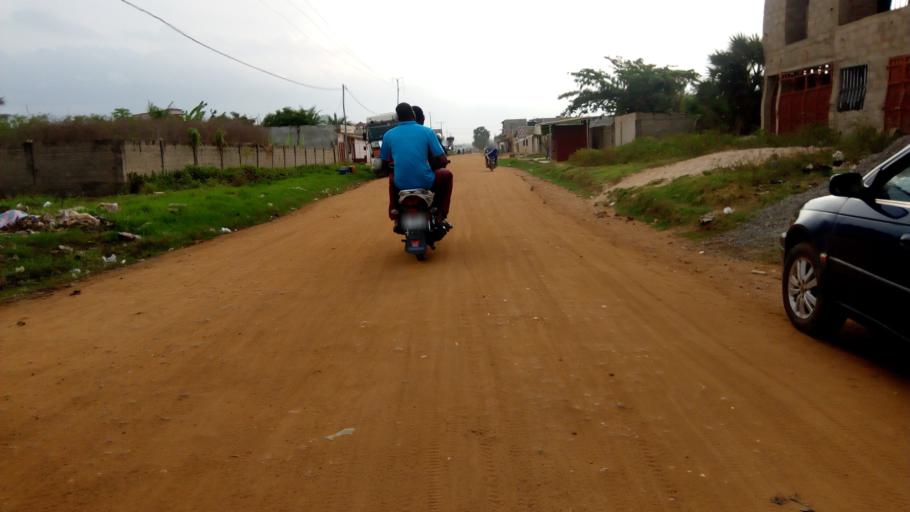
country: TG
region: Maritime
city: Lome
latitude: 6.2520
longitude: 1.2153
